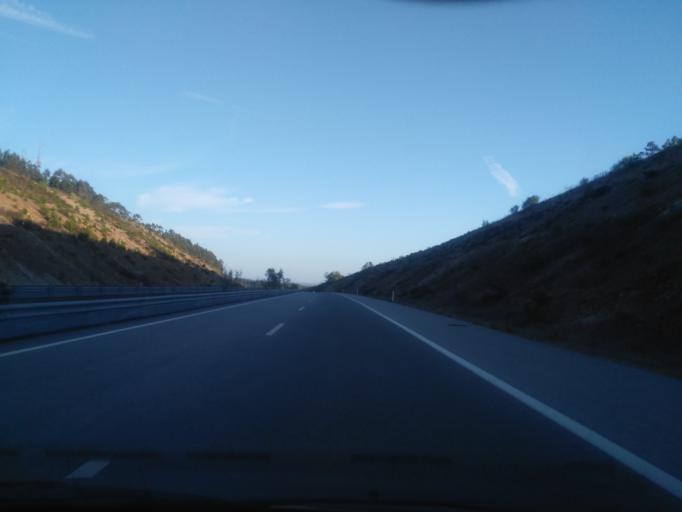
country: PT
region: Coimbra
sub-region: Figueira da Foz
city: Alhadas
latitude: 40.1878
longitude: -8.8113
